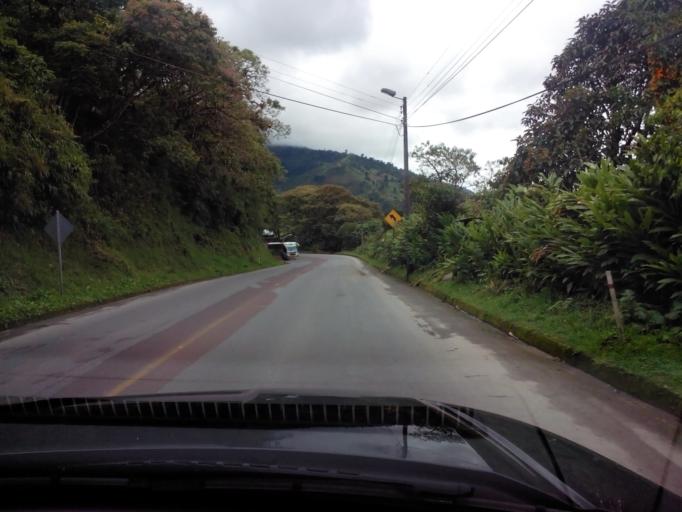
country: EC
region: Napo
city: Archidona
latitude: -0.4637
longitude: -77.8937
